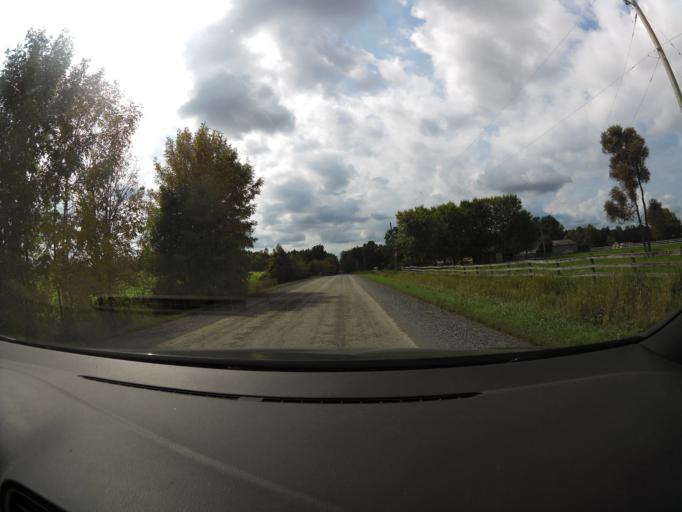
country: CA
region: Ontario
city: Arnprior
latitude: 45.3973
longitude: -76.2393
